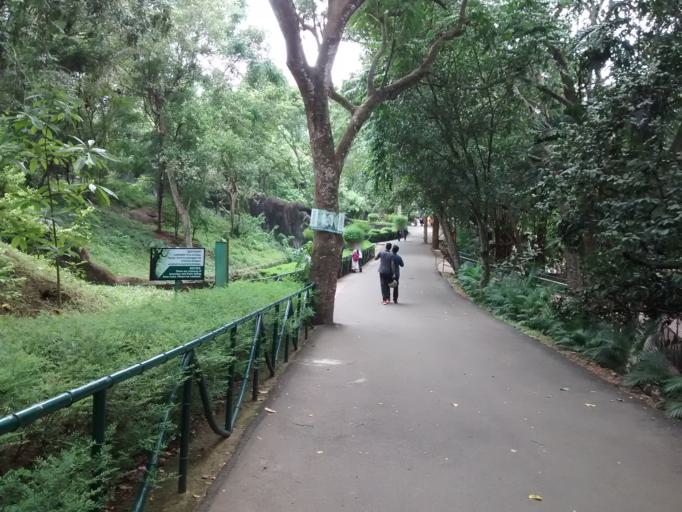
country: IN
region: Kerala
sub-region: Thiruvananthapuram
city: Thiruvananthapuram
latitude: 8.5104
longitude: 76.9553
